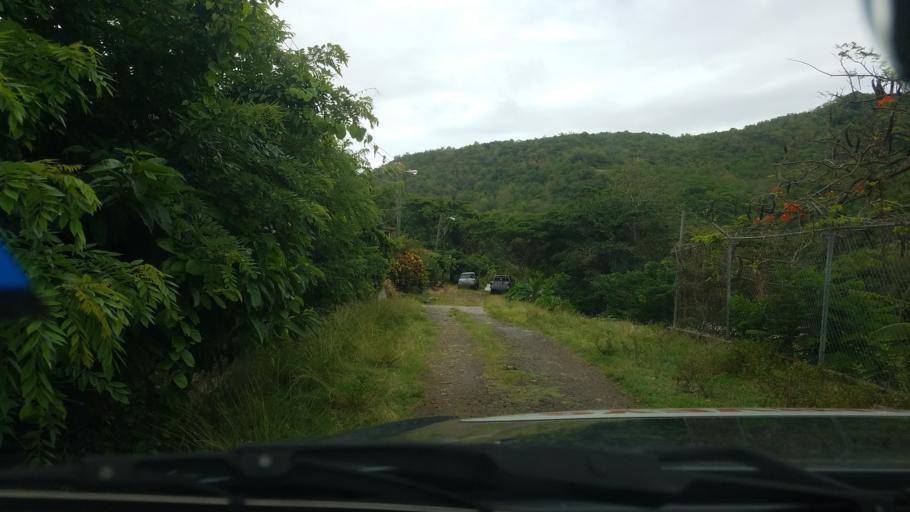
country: LC
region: Castries Quarter
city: Bisee
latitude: 14.0122
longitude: -60.9188
